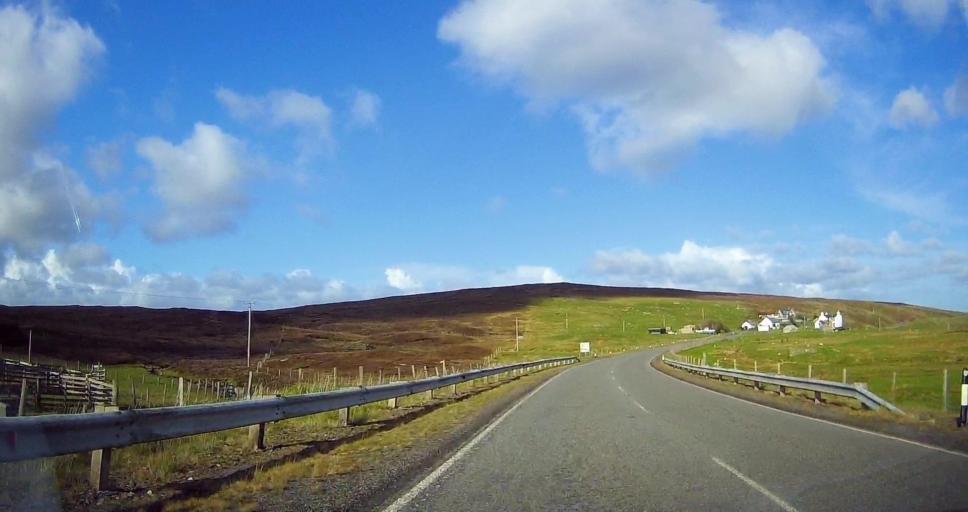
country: GB
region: Scotland
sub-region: Shetland Islands
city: Lerwick
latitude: 60.3526
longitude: -1.2041
